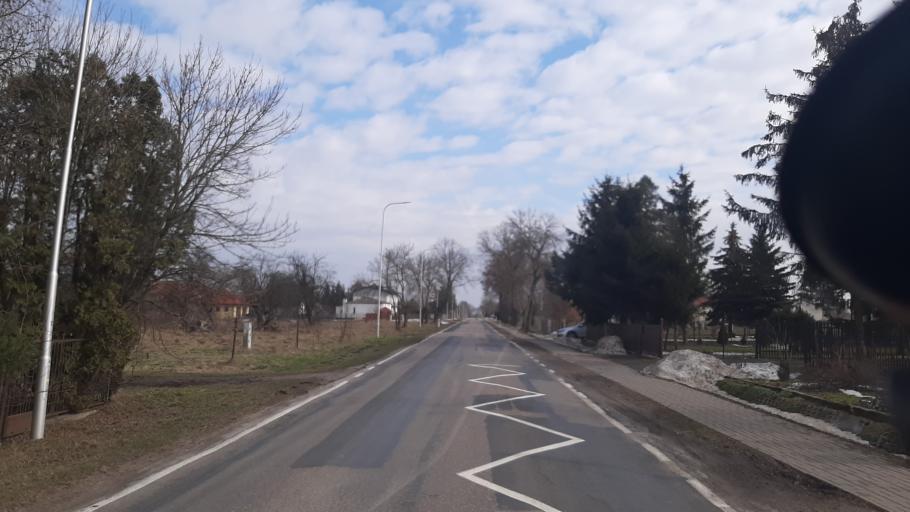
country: PL
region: Lublin Voivodeship
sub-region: Powiat lubelski
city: Niemce
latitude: 51.3616
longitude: 22.5782
